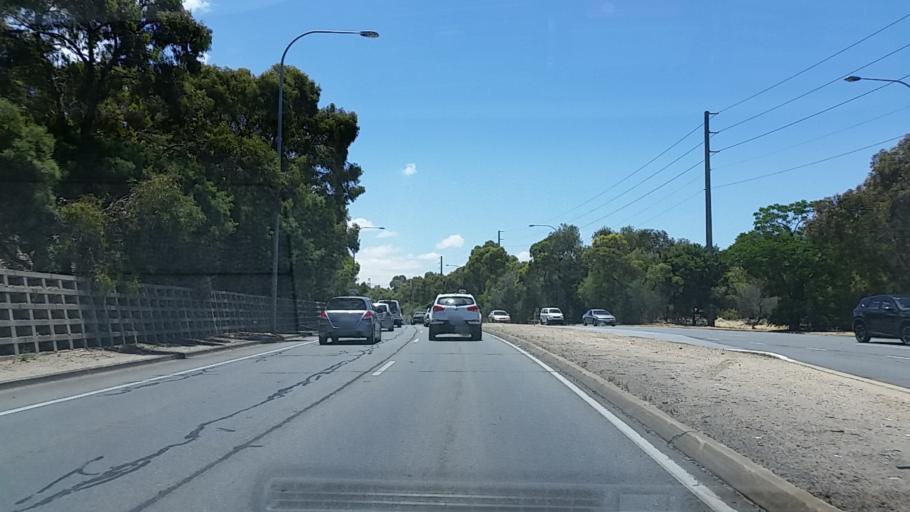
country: AU
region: South Australia
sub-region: Salisbury
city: Salisbury
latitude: -34.7631
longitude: 138.6407
